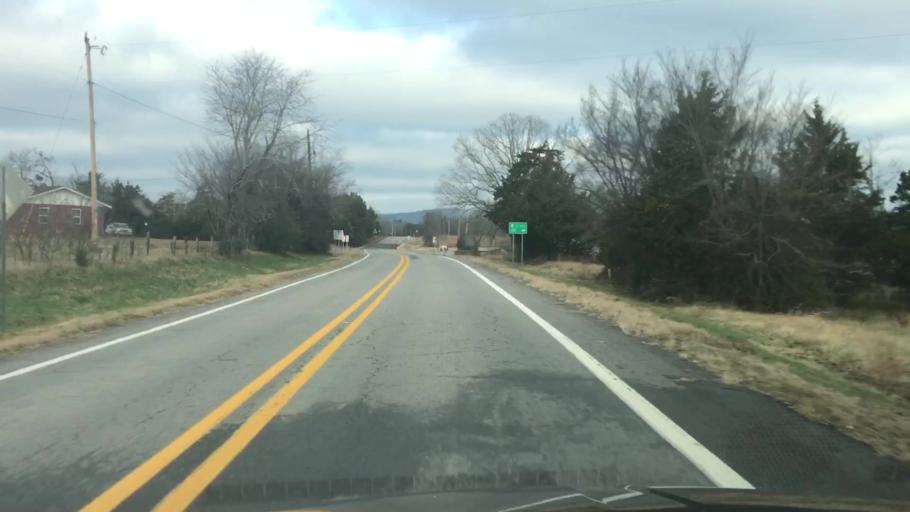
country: US
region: Arkansas
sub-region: Montgomery County
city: Mount Ida
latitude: 34.6330
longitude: -93.7362
